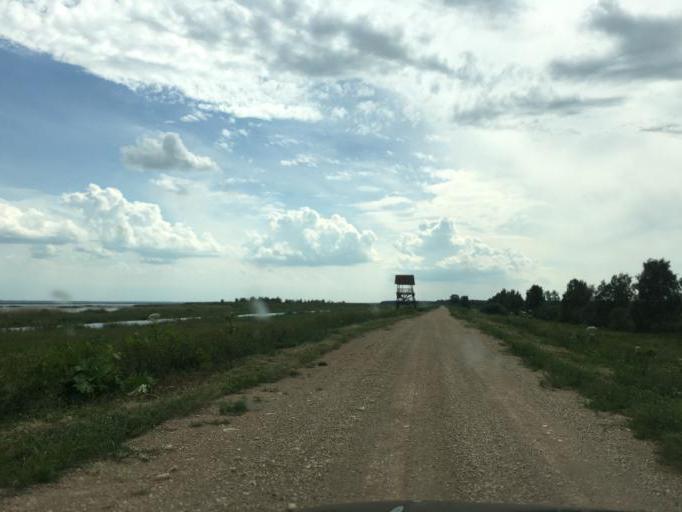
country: LV
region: Lubana
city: Lubana
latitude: 56.7916
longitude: 26.8230
